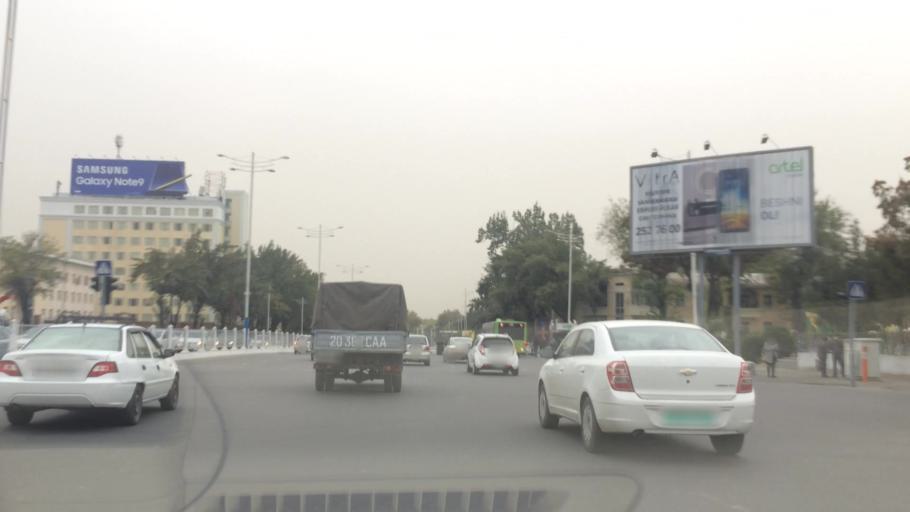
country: UZ
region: Toshkent Shahri
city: Tashkent
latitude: 41.3055
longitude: 69.3069
